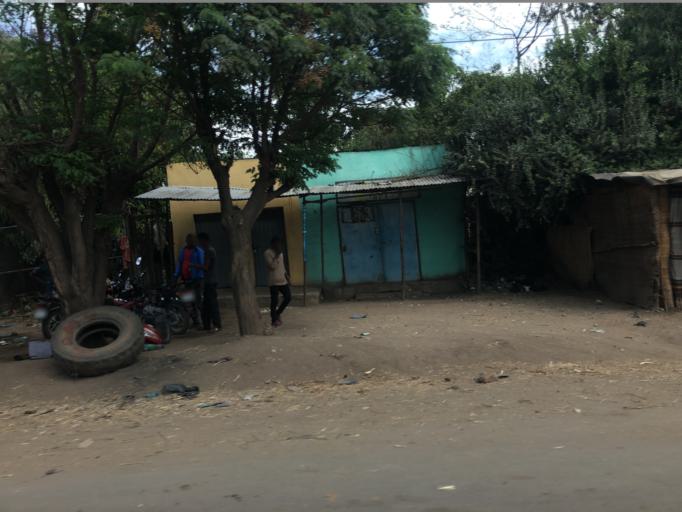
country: ET
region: Oromiya
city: Shashemene
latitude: 7.3653
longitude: 38.6713
